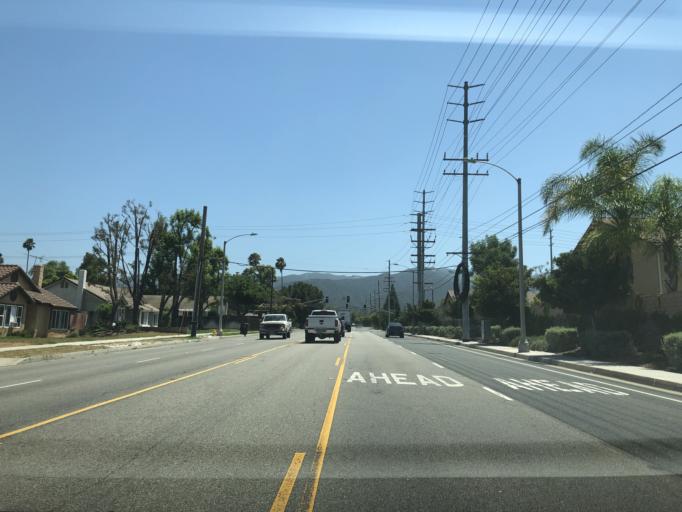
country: US
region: California
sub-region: Riverside County
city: Corona
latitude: 33.8594
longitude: -117.5859
